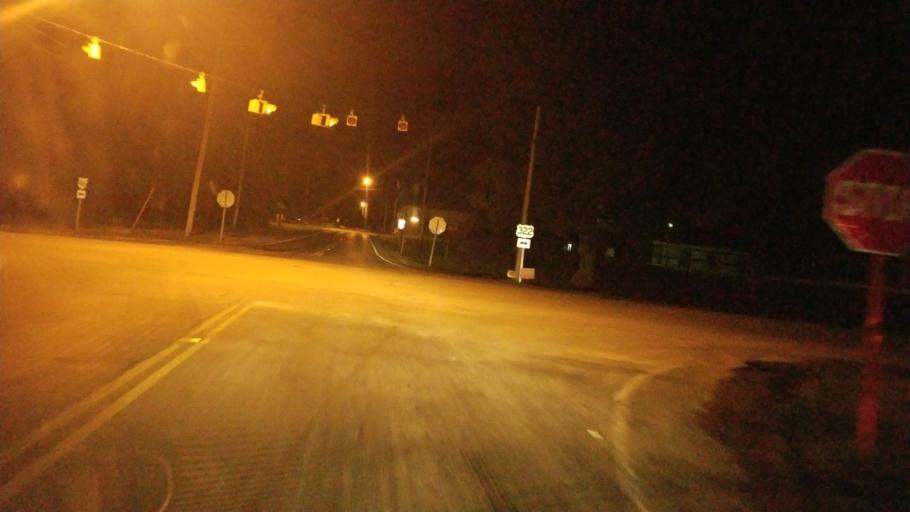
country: US
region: Ohio
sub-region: Ashtabula County
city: Orwell
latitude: 41.5356
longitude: -80.7625
